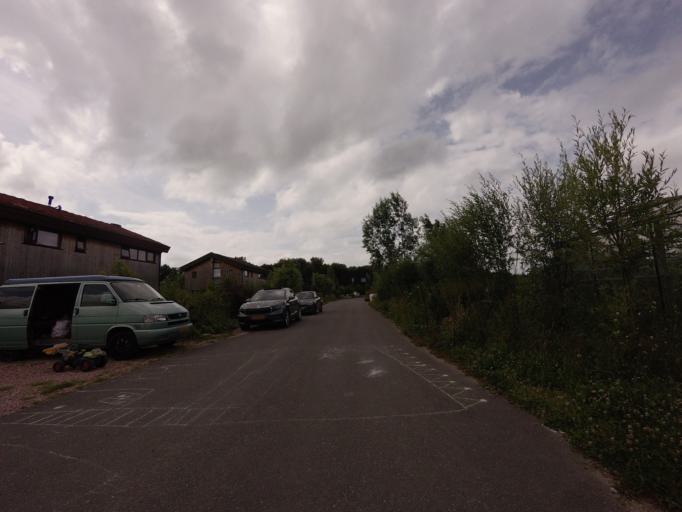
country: NL
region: North Holland
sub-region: Gemeente Huizen
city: Huizen
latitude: 52.3309
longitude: 5.3158
